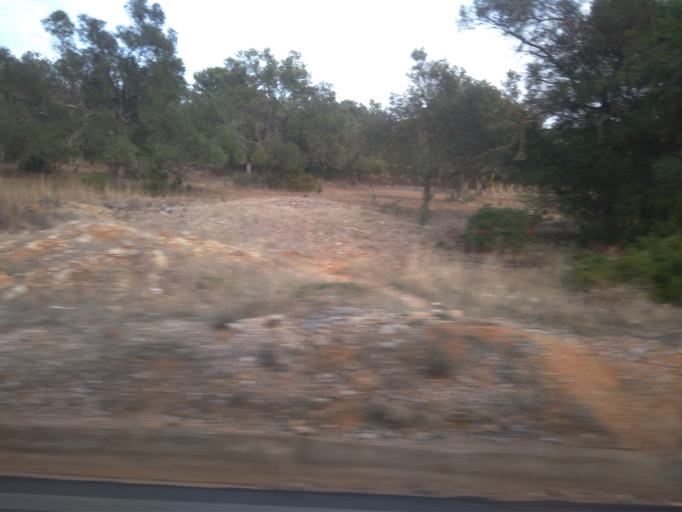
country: PT
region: Faro
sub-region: Faro
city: Santa Barbara de Nexe
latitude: 37.0924
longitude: -7.9622
